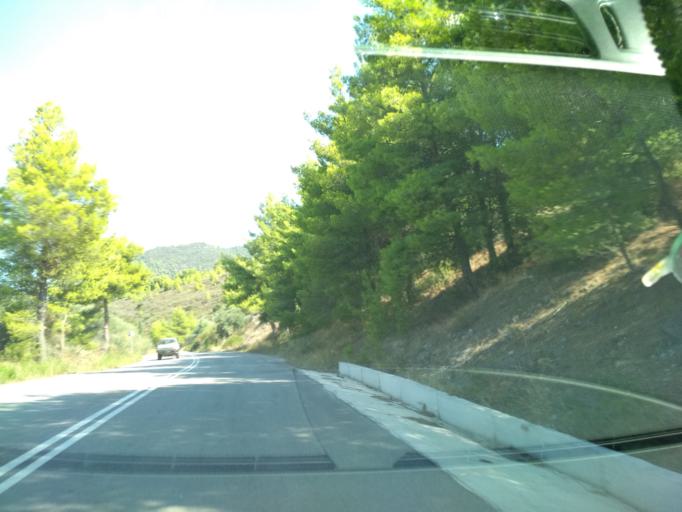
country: GR
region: Central Greece
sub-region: Nomos Evvoias
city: Roviai
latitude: 38.8184
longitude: 23.2302
